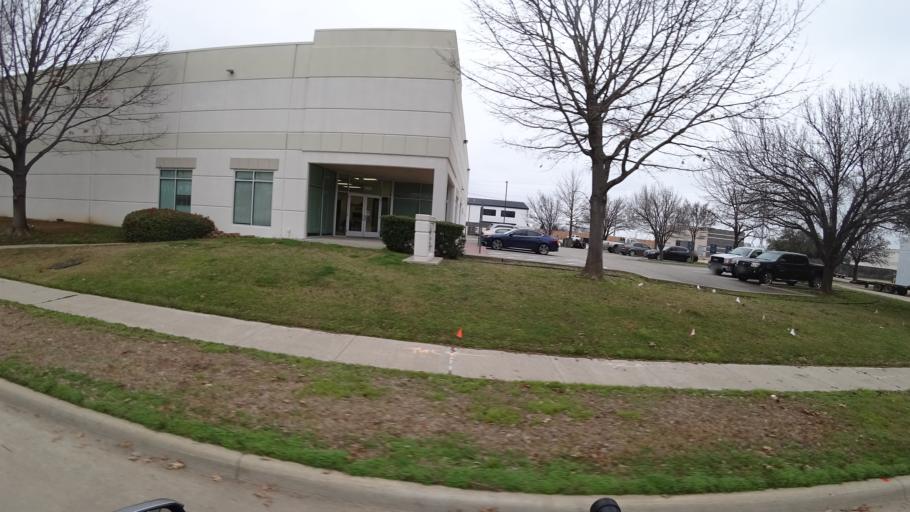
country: US
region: Texas
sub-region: Denton County
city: Lewisville
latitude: 33.0642
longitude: -97.0085
